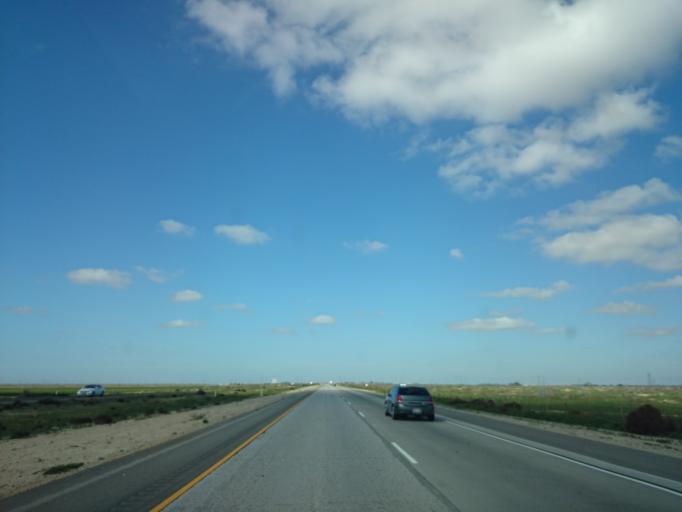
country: US
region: California
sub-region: Kern County
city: Buttonwillow
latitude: 35.3656
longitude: -119.3507
